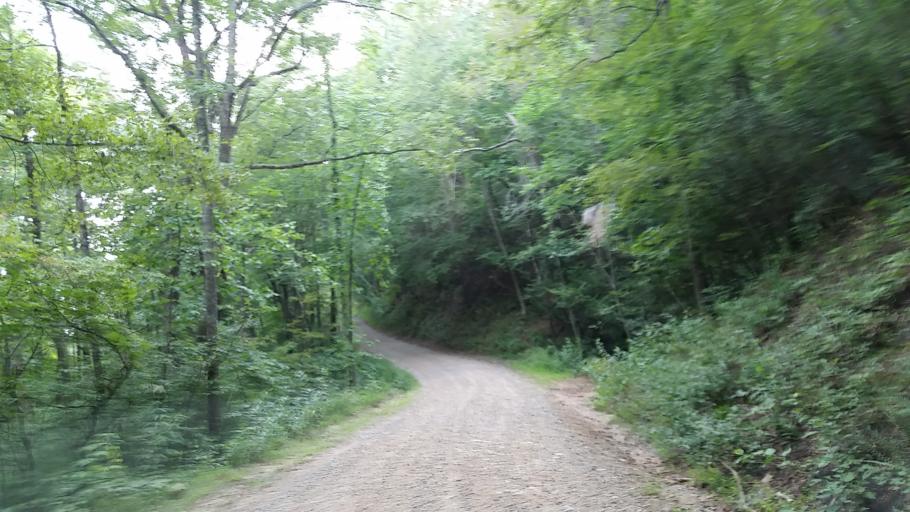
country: US
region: Georgia
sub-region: Lumpkin County
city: Dahlonega
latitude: 34.6509
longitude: -84.0690
